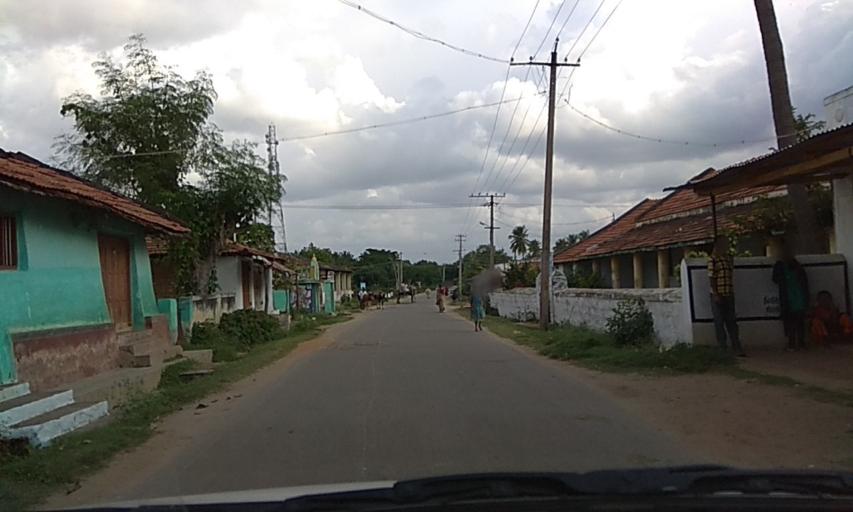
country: IN
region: Karnataka
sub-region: Chamrajnagar
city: Gundlupet
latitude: 11.8900
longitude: 76.7464
